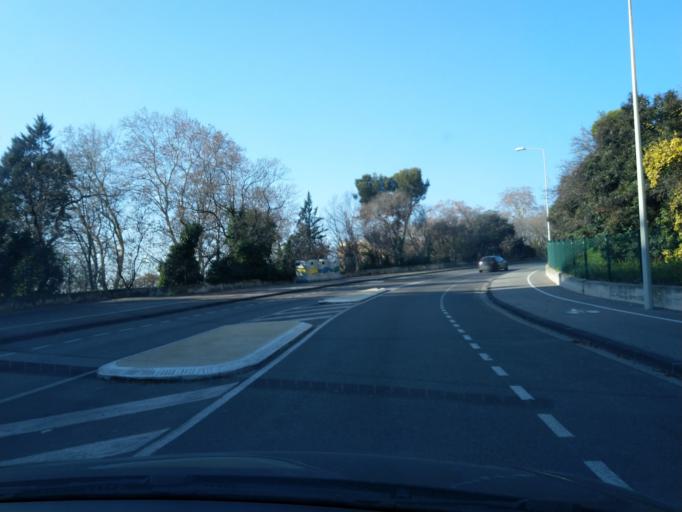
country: FR
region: Provence-Alpes-Cote d'Azur
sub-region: Departement des Bouches-du-Rhone
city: Marseille 12
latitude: 43.3022
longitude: 5.4299
